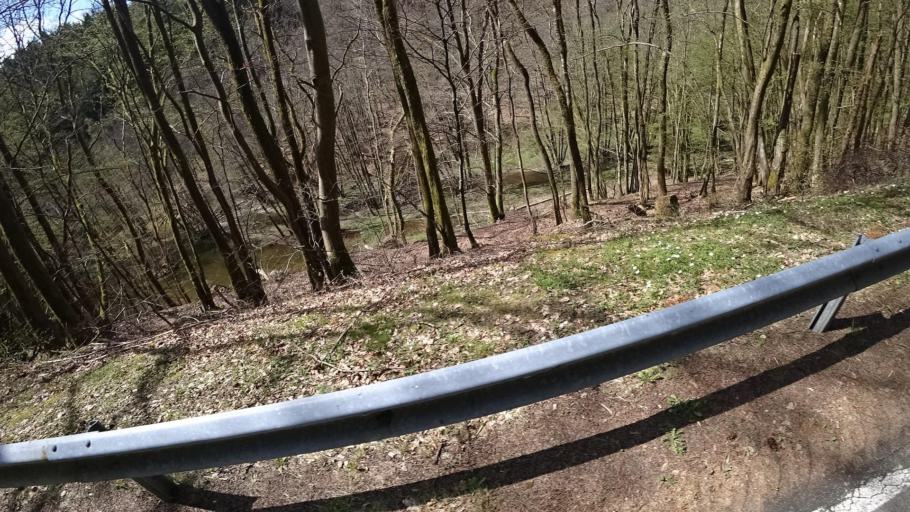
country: DE
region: Rheinland-Pfalz
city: Grimburg
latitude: 49.6258
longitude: 6.8728
